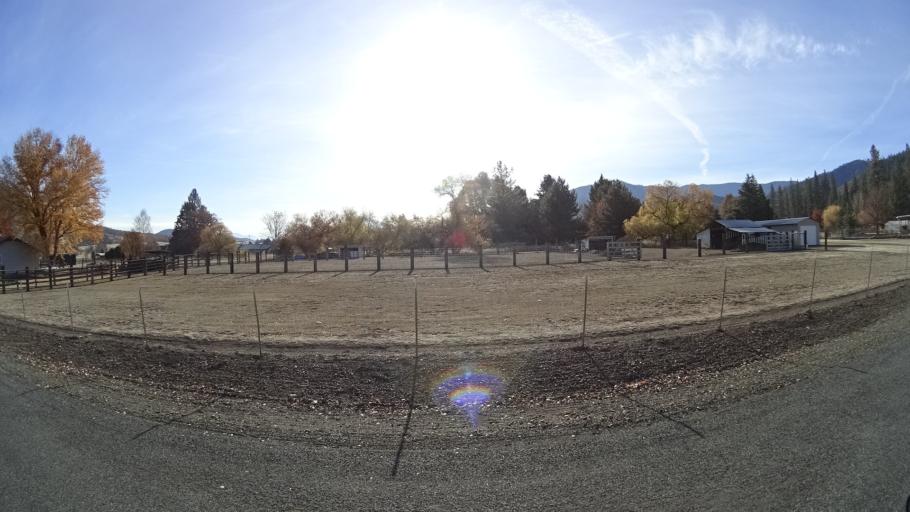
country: US
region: California
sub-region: Siskiyou County
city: Yreka
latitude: 41.6804
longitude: -122.6377
